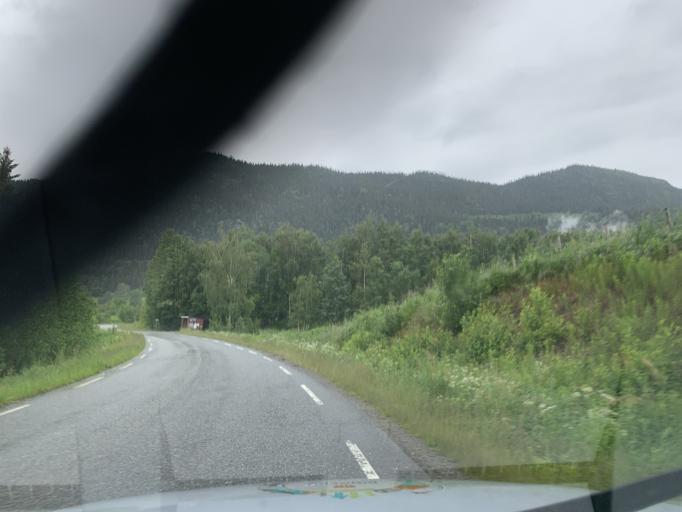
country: NO
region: Oppland
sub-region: Ringebu
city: Ringebu
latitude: 61.4490
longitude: 10.1736
